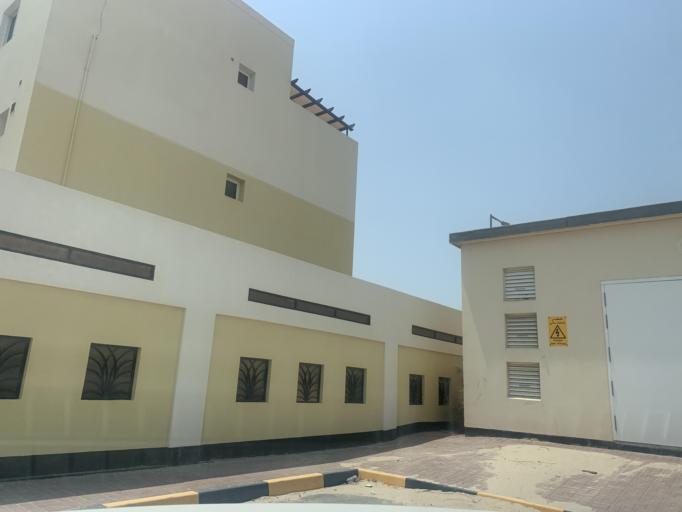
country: BH
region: Central Governorate
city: Madinat Hamad
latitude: 26.1370
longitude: 50.4692
